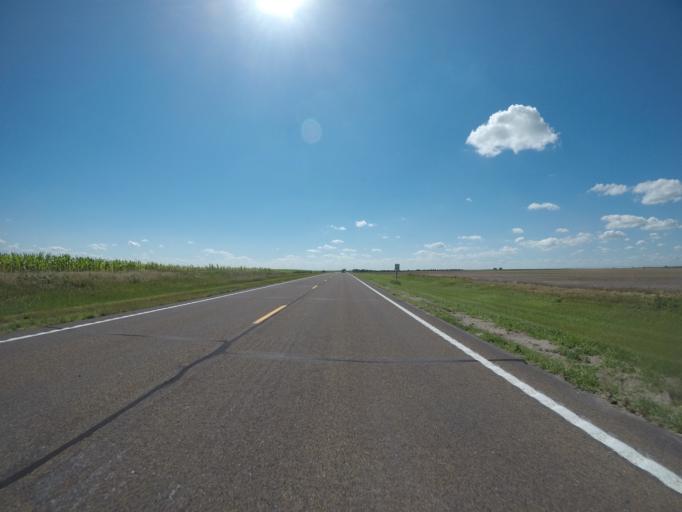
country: US
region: Nebraska
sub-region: Chase County
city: Imperial
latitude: 40.5378
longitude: -101.9147
